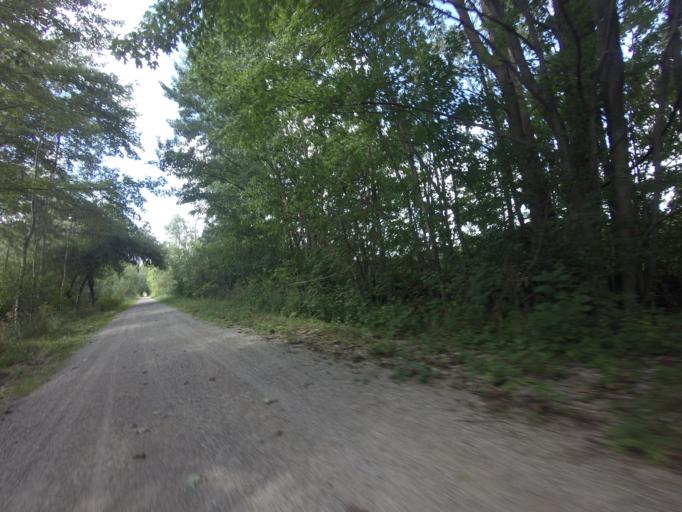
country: CA
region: Ontario
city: Huron East
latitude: 43.6172
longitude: -81.1467
